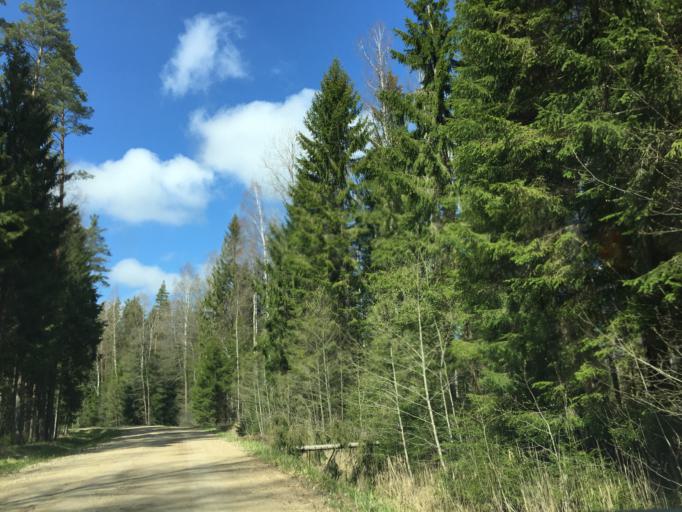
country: EE
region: Valgamaa
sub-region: Valga linn
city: Valga
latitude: 57.5929
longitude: 26.0839
